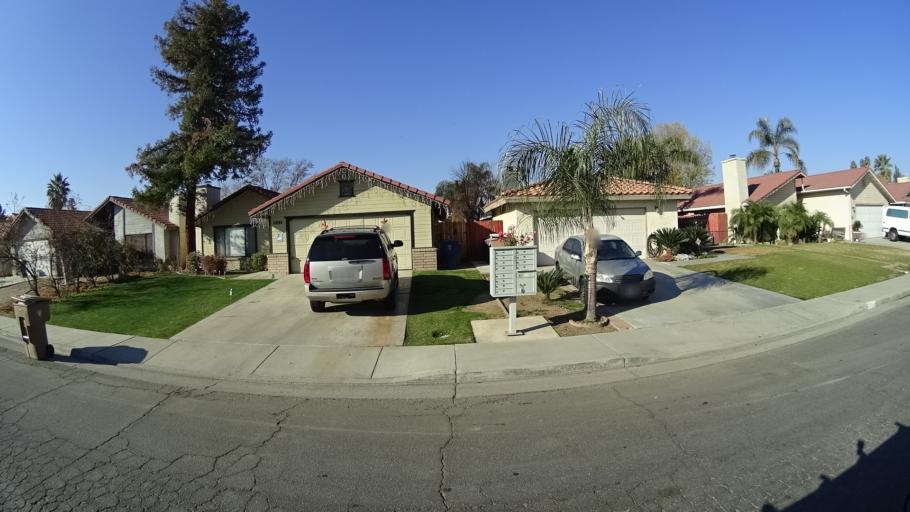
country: US
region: California
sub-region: Kern County
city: Greenfield
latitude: 35.3093
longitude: -119.0103
